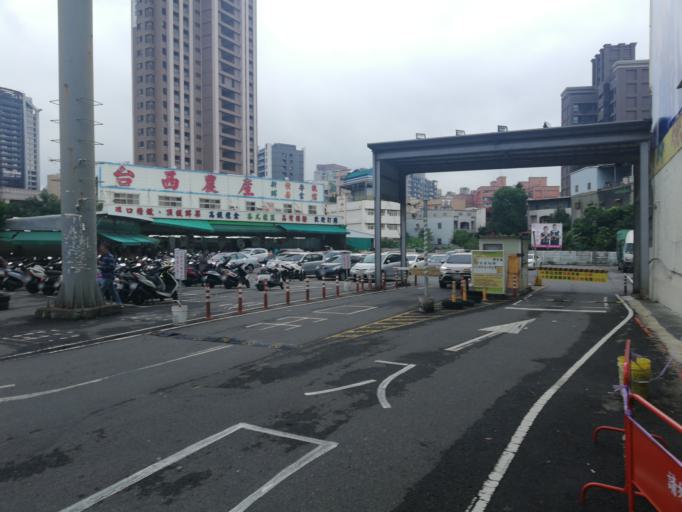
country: TW
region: Taiwan
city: Taoyuan City
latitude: 25.0083
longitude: 121.3026
